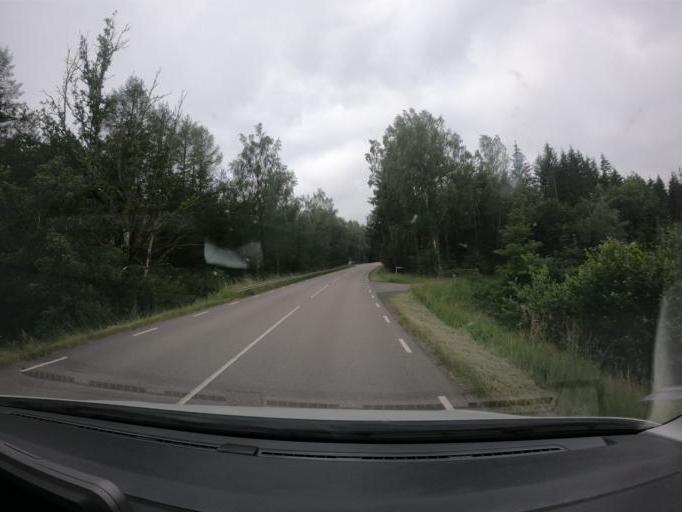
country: SE
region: Skane
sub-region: Perstorps Kommun
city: Perstorp
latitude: 56.1205
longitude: 13.4010
